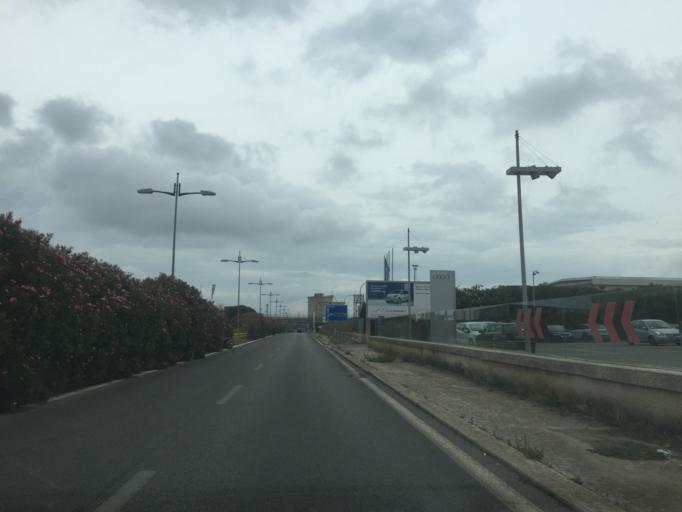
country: IT
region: Sicily
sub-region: Ragusa
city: Ragusa
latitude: 36.8882
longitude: 14.6905
